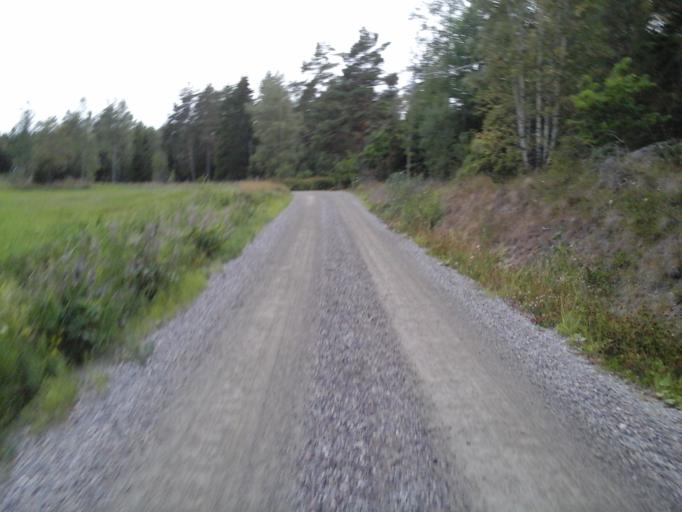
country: SE
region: Soedermanland
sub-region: Eskilstuna Kommun
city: Arla
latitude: 59.2486
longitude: 16.7796
